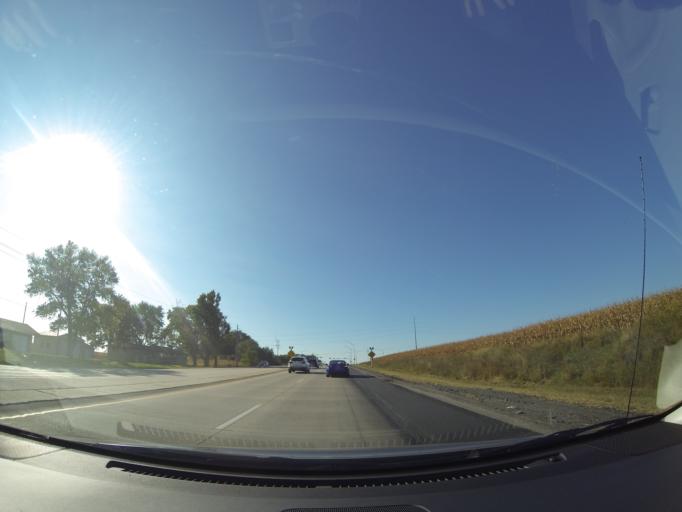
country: US
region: Nebraska
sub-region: Sarpy County
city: Gretna
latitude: 41.2074
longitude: -96.2344
